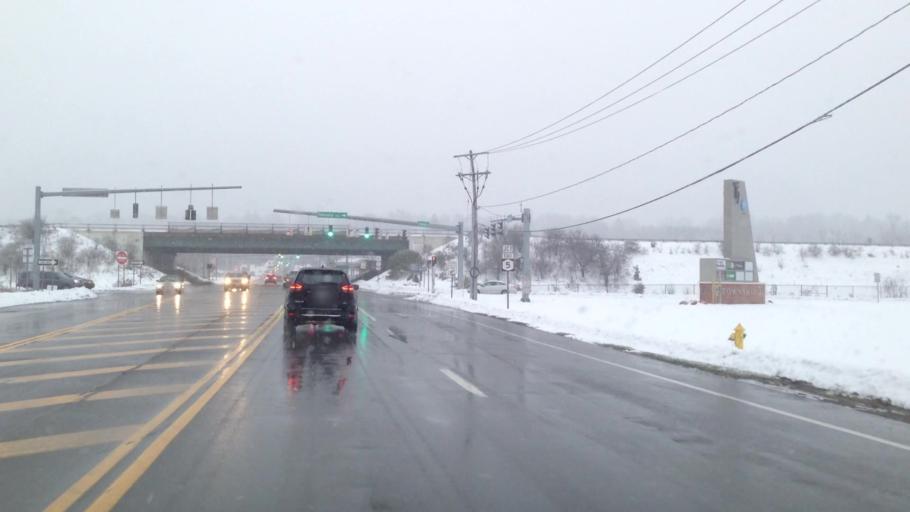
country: US
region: New York
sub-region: Onondaga County
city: Fairmount
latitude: 43.0561
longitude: -76.2661
